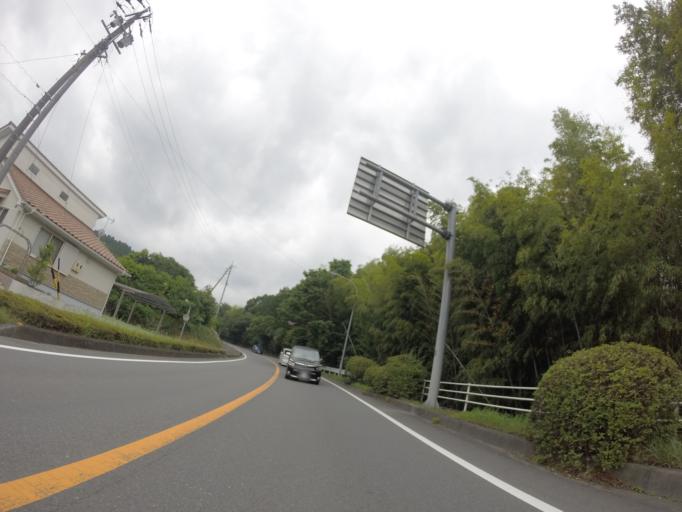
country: JP
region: Shizuoka
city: Fujinomiya
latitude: 35.1948
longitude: 138.5877
